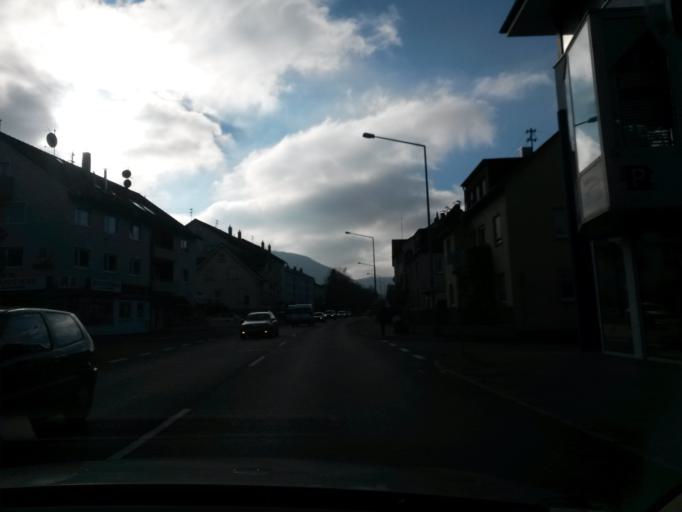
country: DE
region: Baden-Wuerttemberg
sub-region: Regierungsbezirk Stuttgart
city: Geislingen an der Steige
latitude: 48.6220
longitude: 9.8227
